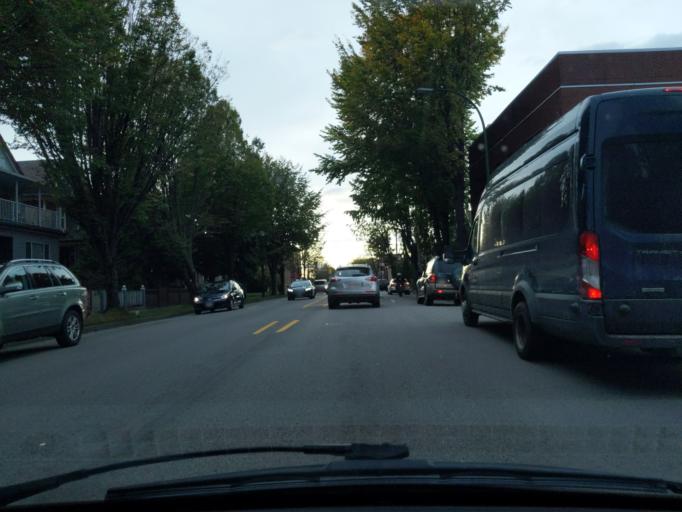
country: CA
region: British Columbia
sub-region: Fraser Valley Regional District
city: North Vancouver
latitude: 49.2696
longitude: -123.0675
